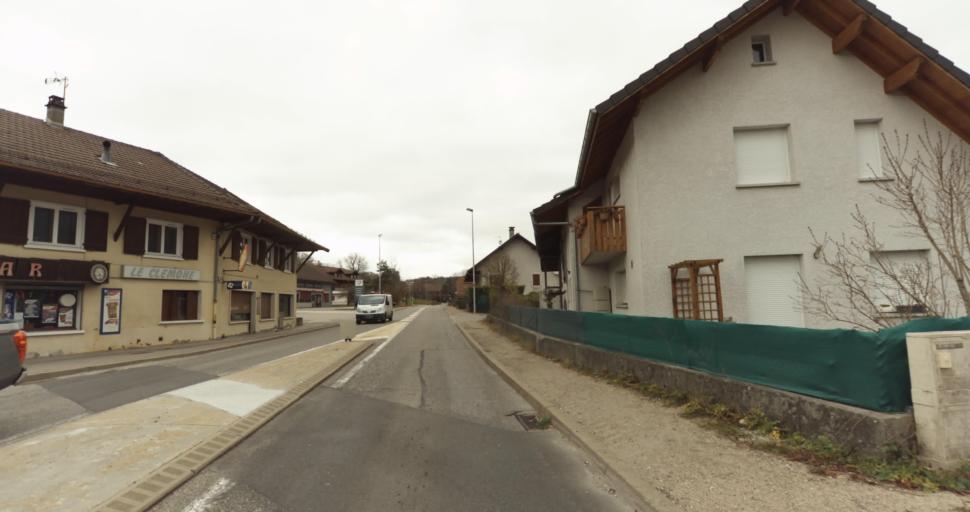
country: FR
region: Rhone-Alpes
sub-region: Departement de la Haute-Savoie
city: Saint-Martin-Bellevue
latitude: 45.9778
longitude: 6.1643
